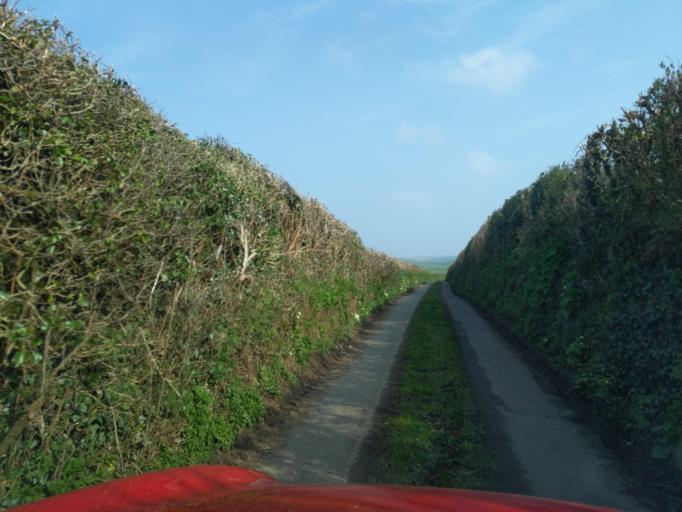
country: GB
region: England
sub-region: Devon
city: Kingsbridge
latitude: 50.3082
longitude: -3.7678
